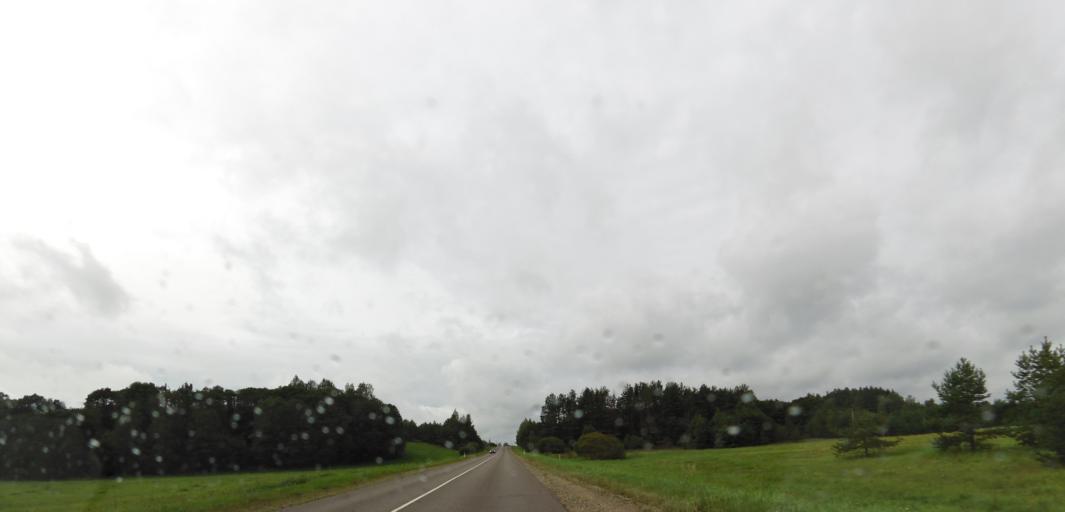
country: LT
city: Moletai
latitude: 55.2125
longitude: 25.3331
